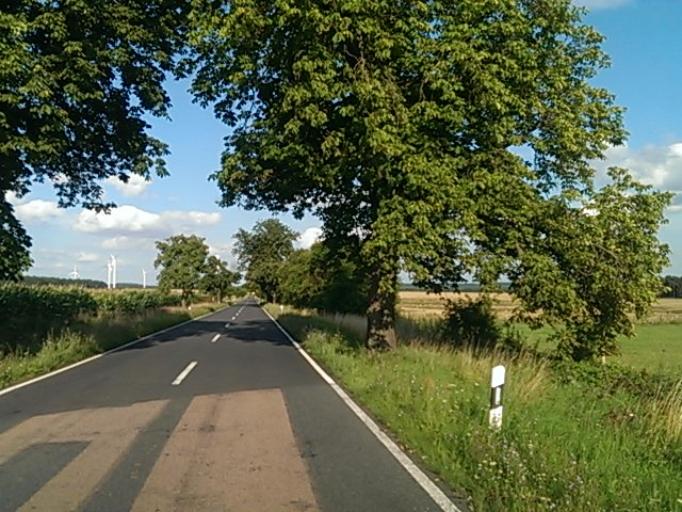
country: DE
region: Saxony-Anhalt
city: Nudersdorf
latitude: 51.9648
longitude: 12.5770
